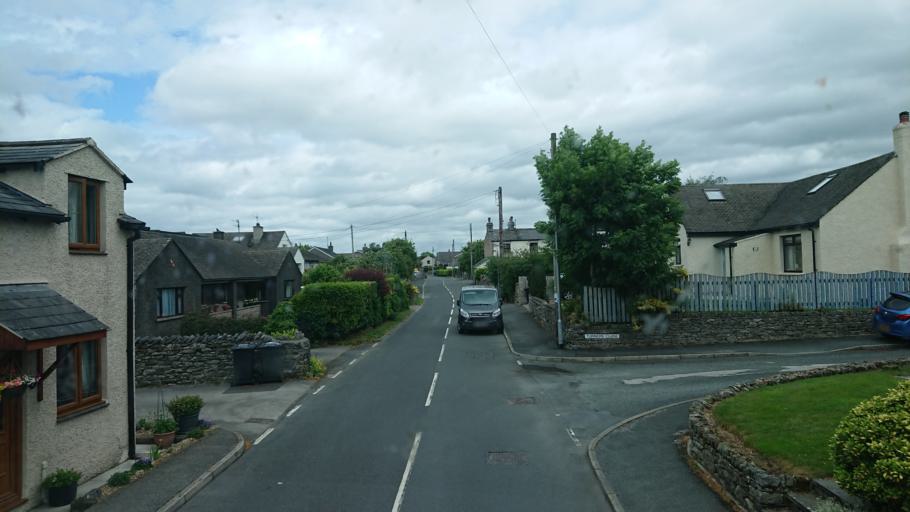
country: GB
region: England
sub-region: Cumbria
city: Milnthorpe
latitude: 54.2071
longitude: -2.7294
